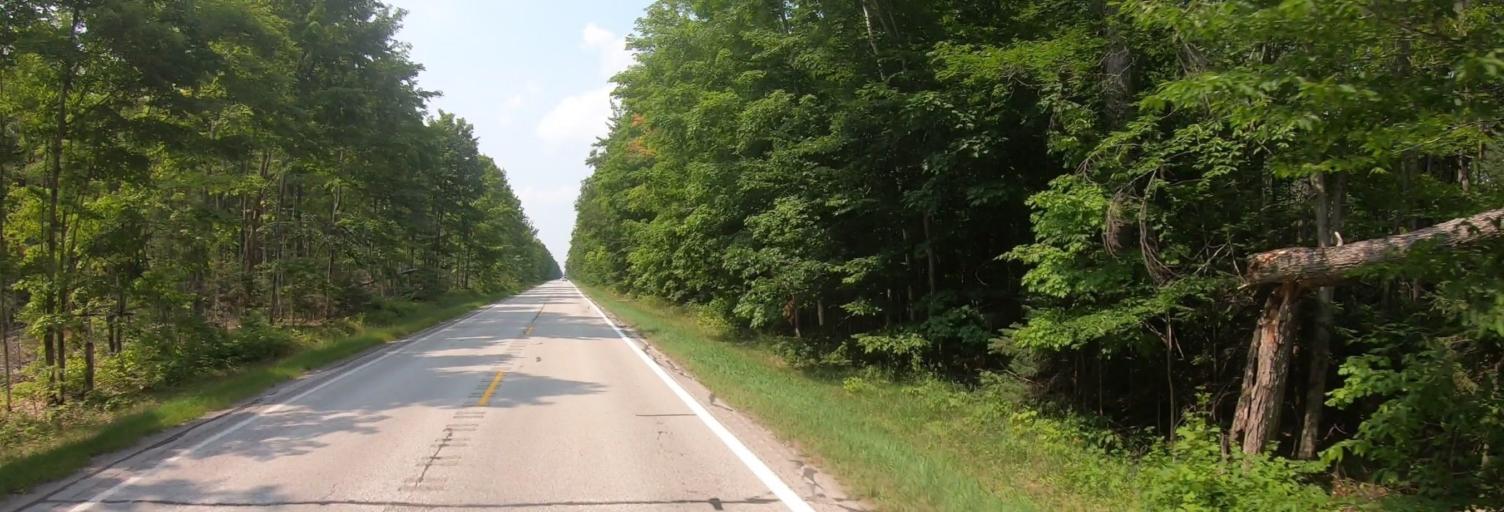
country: US
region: Michigan
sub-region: Luce County
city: Newberry
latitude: 46.5510
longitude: -85.3714
